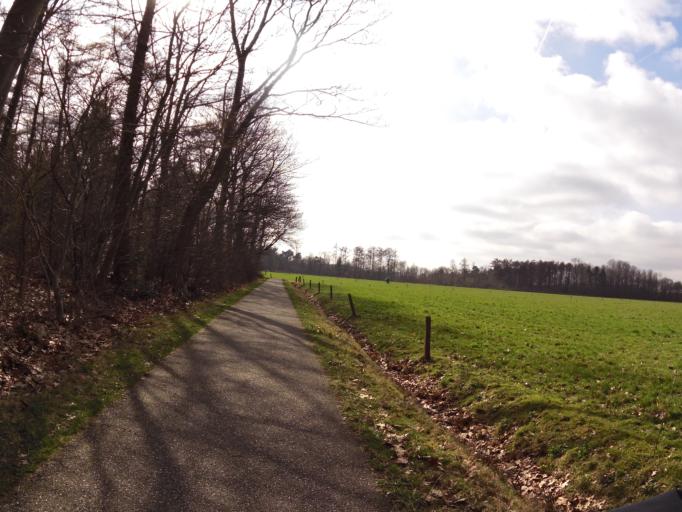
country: NL
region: Friesland
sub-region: Gemeente Weststellingwerf
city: Noordwolde
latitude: 52.8761
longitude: 6.2076
